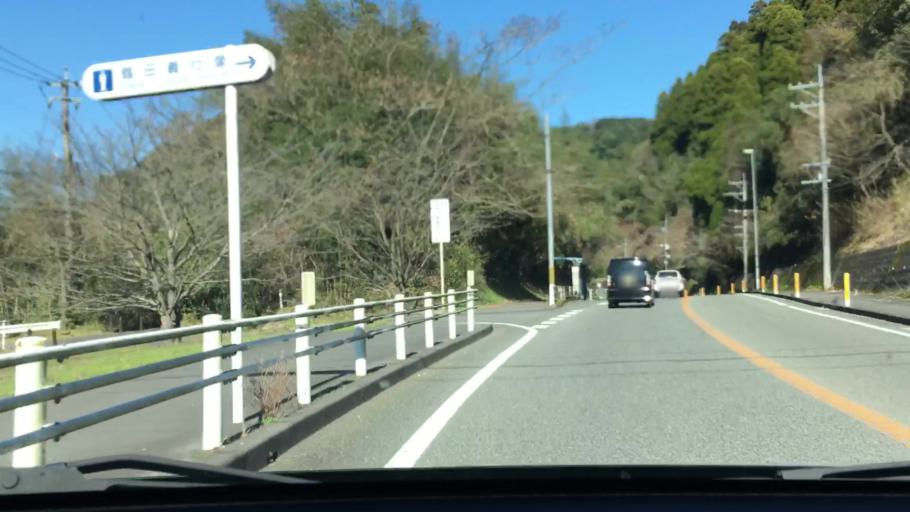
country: JP
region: Kagoshima
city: Kagoshima-shi
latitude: 31.6367
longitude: 130.5193
